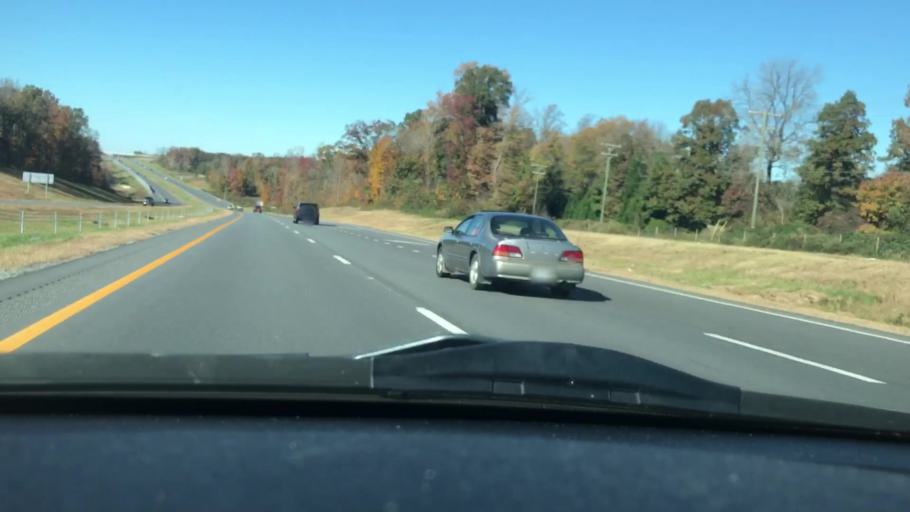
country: US
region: North Carolina
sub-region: Guilford County
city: Summerfield
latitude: 36.2516
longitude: -79.9222
